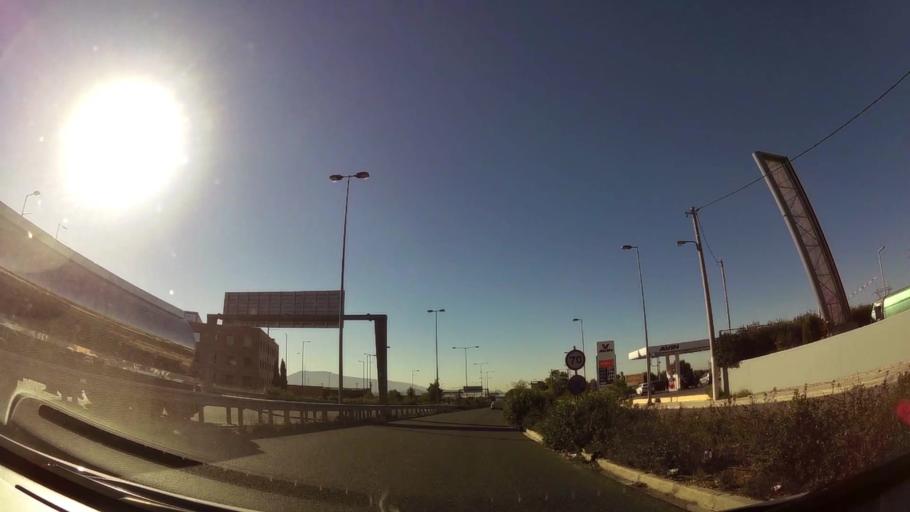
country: GR
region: Attica
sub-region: Nomarchia Anatolikis Attikis
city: Thrakomakedones
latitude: 38.1043
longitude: 23.7642
